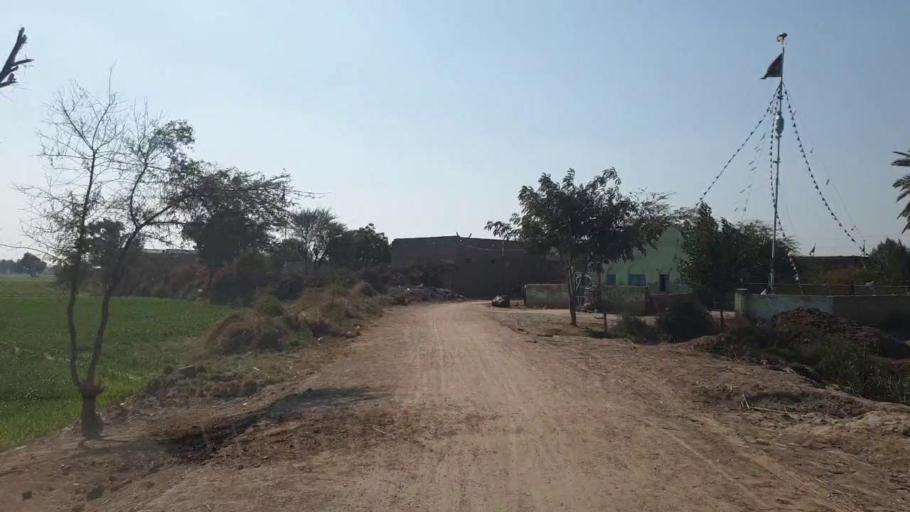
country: PK
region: Sindh
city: Shahdadpur
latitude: 25.9663
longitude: 68.6177
